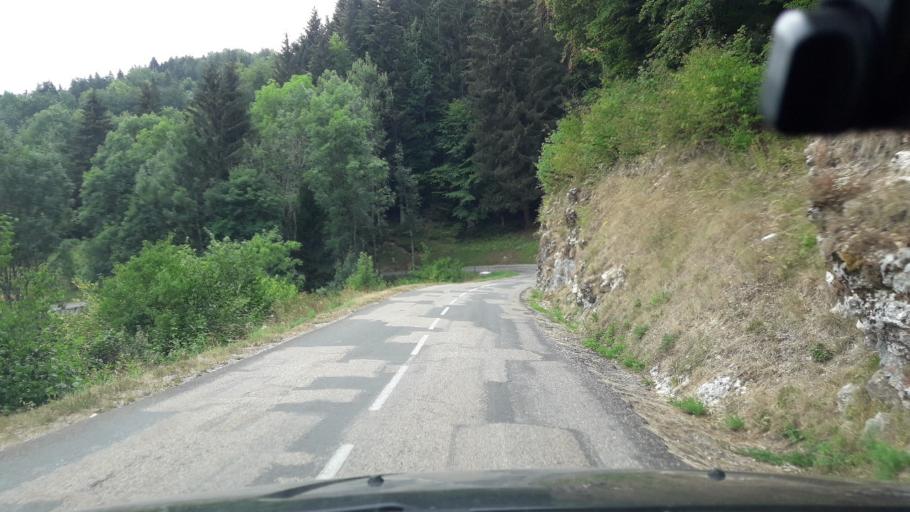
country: FR
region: Rhone-Alpes
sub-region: Departement de la Savoie
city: Vimines
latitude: 45.4473
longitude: 5.8698
